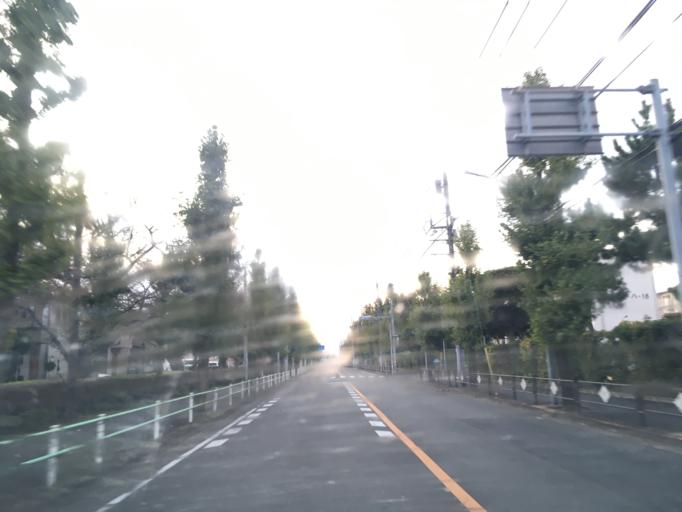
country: JP
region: Tokyo
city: Chofugaoka
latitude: 35.6399
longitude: 139.5586
